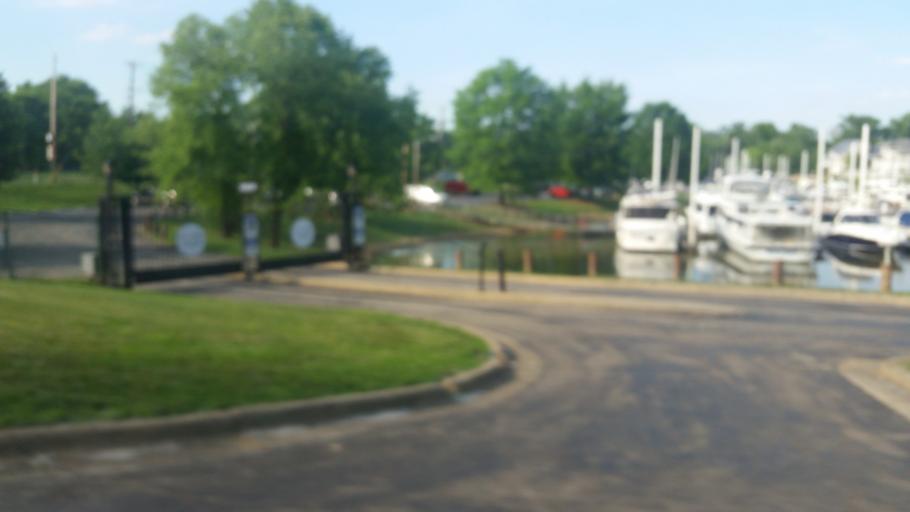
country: US
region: Kentucky
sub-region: Jefferson County
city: Prospect
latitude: 38.3290
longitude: -85.6427
